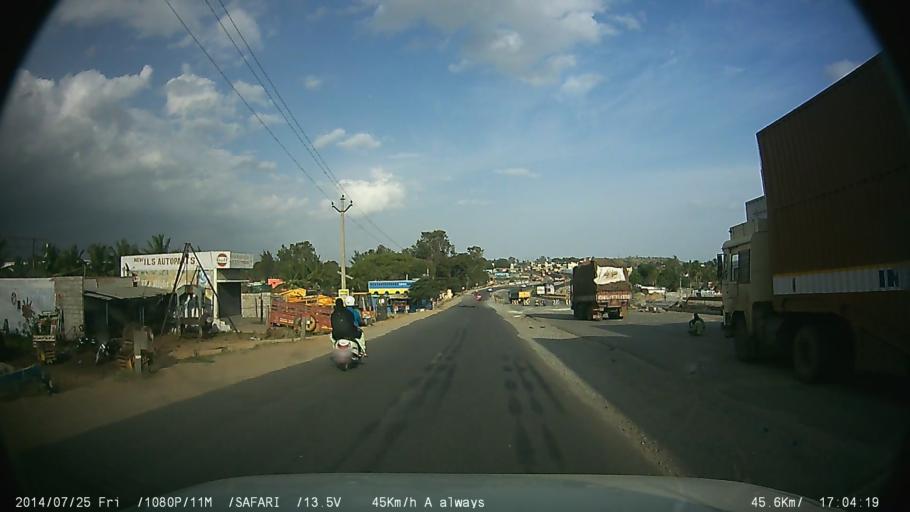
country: IN
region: Tamil Nadu
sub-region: Krishnagiri
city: Hosur
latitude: 12.7151
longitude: 77.8841
